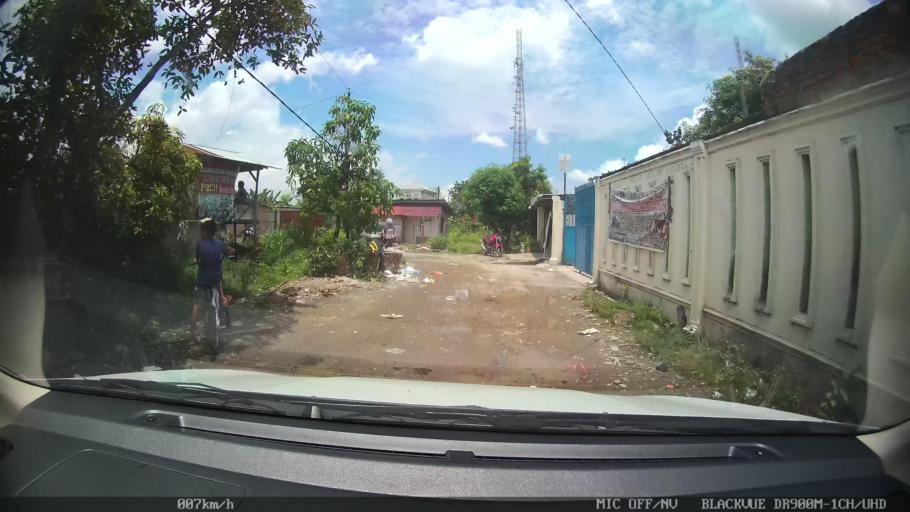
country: ID
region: North Sumatra
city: Medan
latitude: 3.6136
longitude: 98.7210
